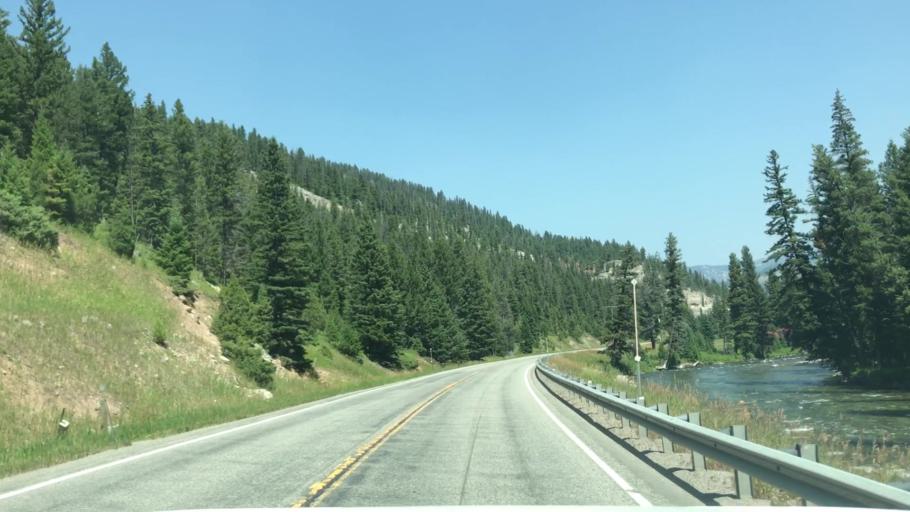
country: US
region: Montana
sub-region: Gallatin County
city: Big Sky
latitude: 45.1612
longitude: -111.2490
